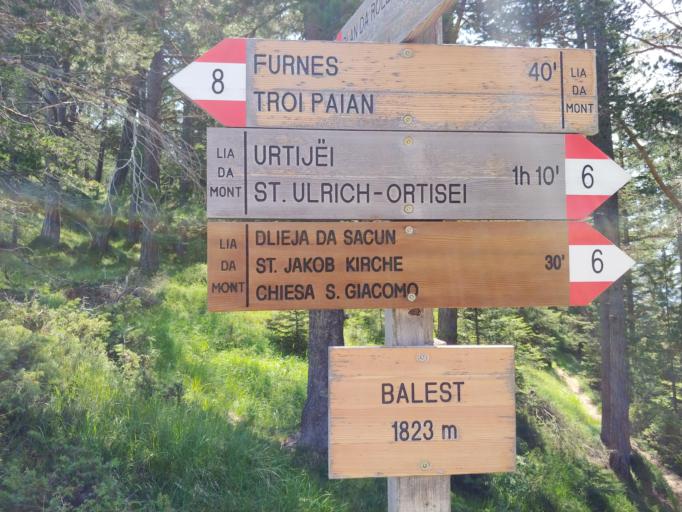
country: IT
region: Trentino-Alto Adige
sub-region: Bolzano
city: Ortisei
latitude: 46.5775
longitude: 11.6983
